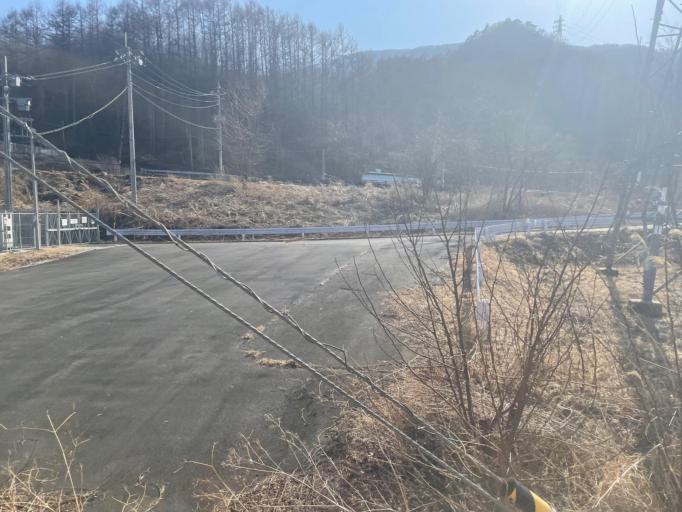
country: JP
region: Gunma
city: Nakanojomachi
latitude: 36.5438
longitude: 138.6572
